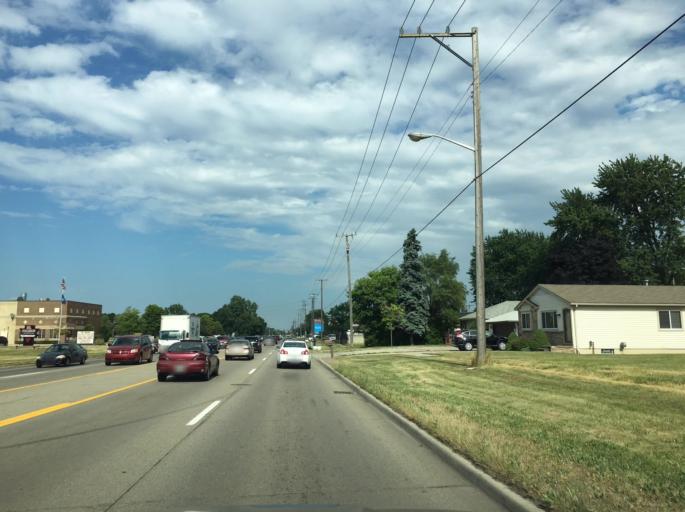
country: US
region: Michigan
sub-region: Macomb County
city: Sterling Heights
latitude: 42.5362
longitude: -83.0452
